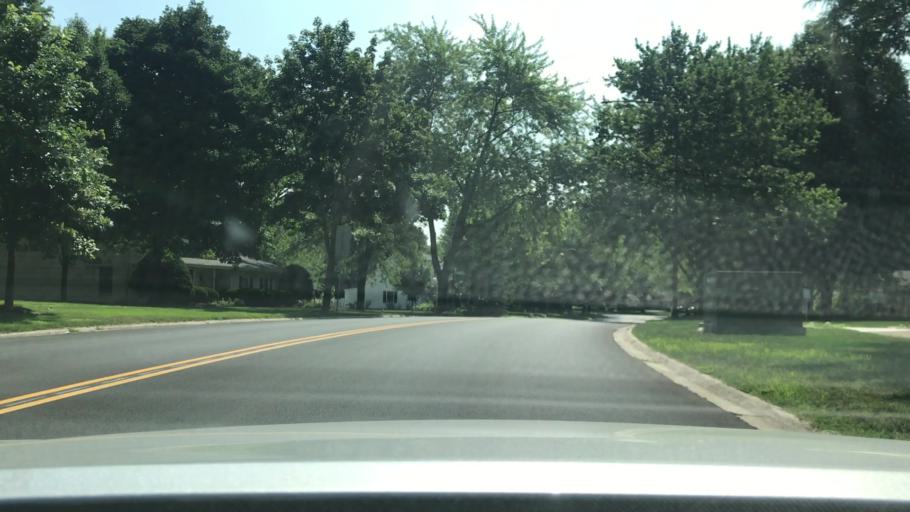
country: US
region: Illinois
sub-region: DuPage County
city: Naperville
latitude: 41.7411
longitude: -88.1326
